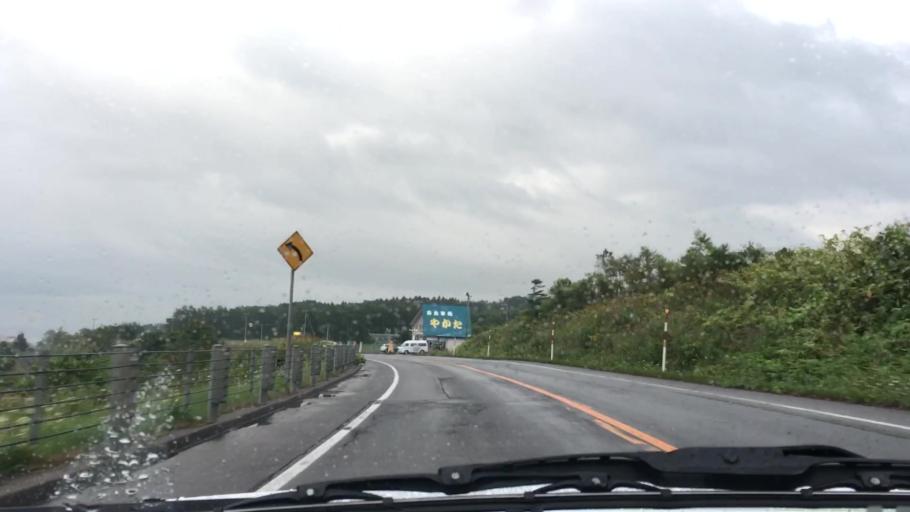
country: JP
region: Hokkaido
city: Nanae
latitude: 42.1795
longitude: 140.4422
